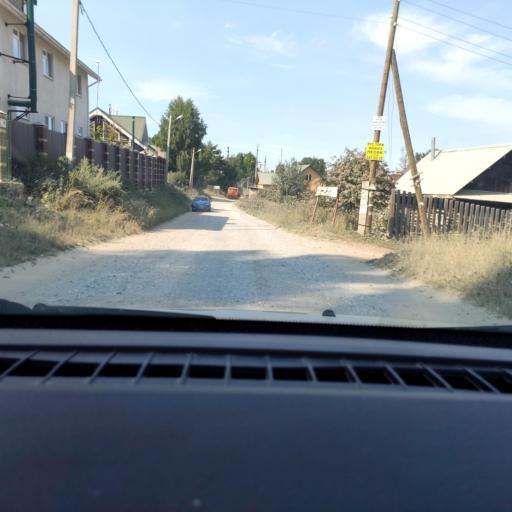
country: RU
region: Perm
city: Polazna
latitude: 58.1357
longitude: 56.4575
